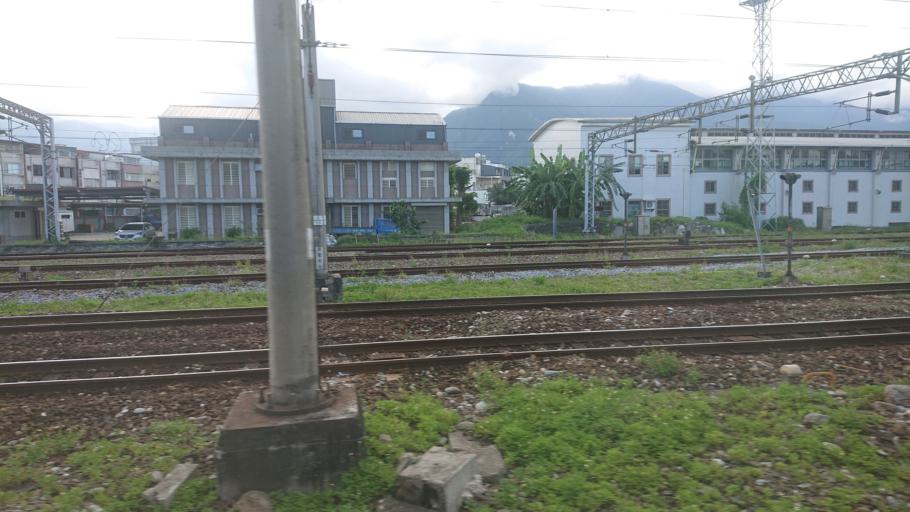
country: TW
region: Taiwan
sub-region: Hualien
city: Hualian
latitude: 23.9905
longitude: 121.5998
